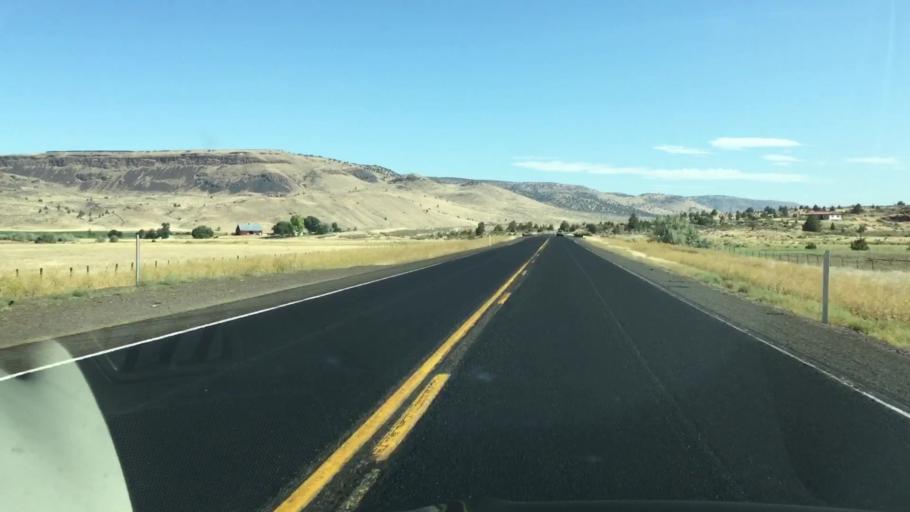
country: US
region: Oregon
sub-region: Jefferson County
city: Madras
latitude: 44.7733
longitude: -120.9690
